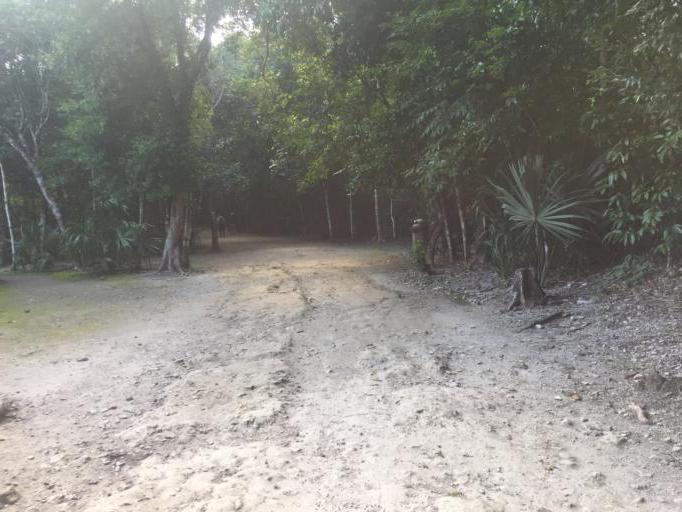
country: MX
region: Quintana Roo
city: Coba
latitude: 20.4931
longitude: -87.7243
